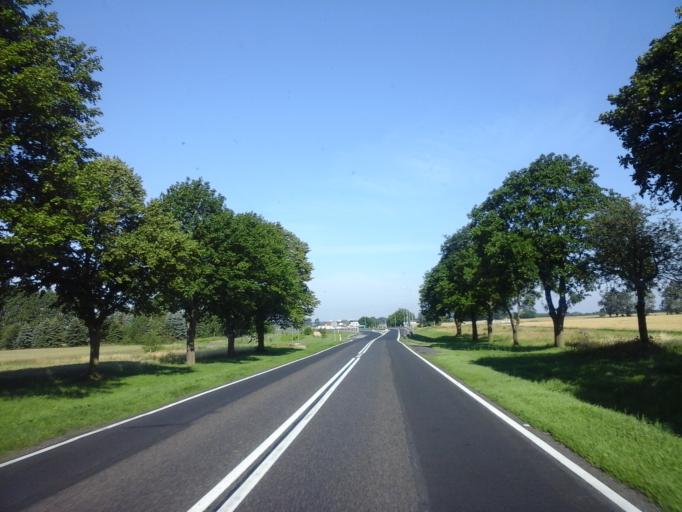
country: PL
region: West Pomeranian Voivodeship
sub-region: Powiat stargardzki
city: Stargard Szczecinski
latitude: 53.3136
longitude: 15.1078
